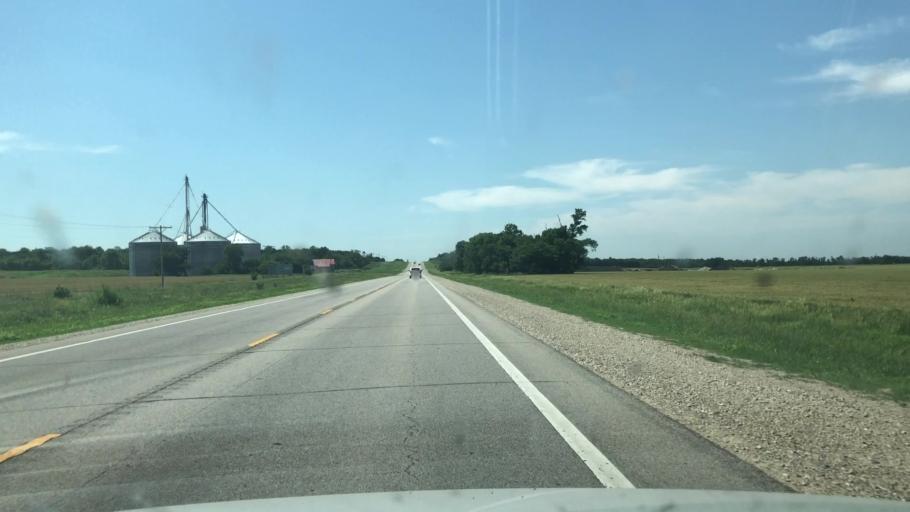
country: US
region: Kansas
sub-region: Butler County
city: Douglass
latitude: 37.3807
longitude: -97.0070
